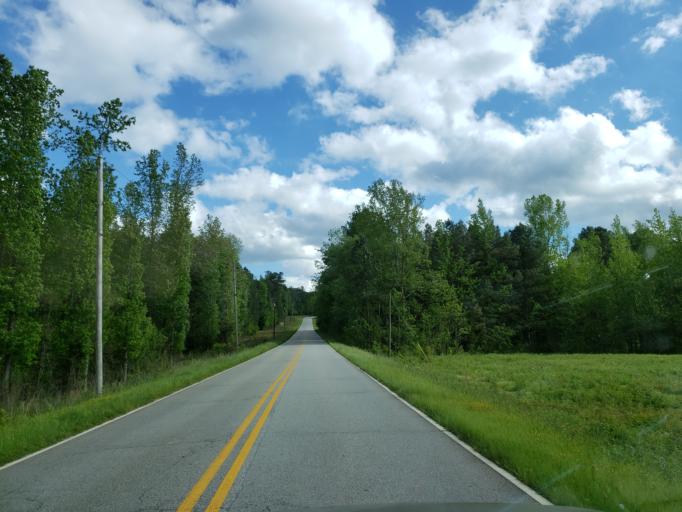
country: US
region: Georgia
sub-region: Carroll County
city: Mount Zion
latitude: 33.6822
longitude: -85.1871
